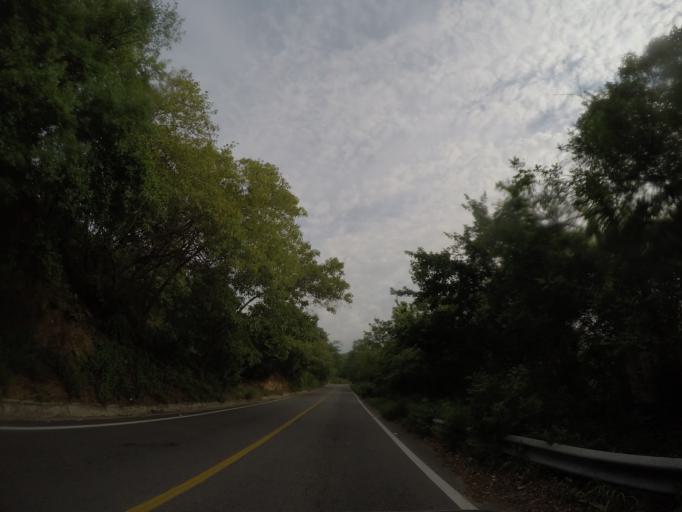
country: MX
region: Oaxaca
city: San Pedro Pochutla
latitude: 15.7001
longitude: -96.4816
